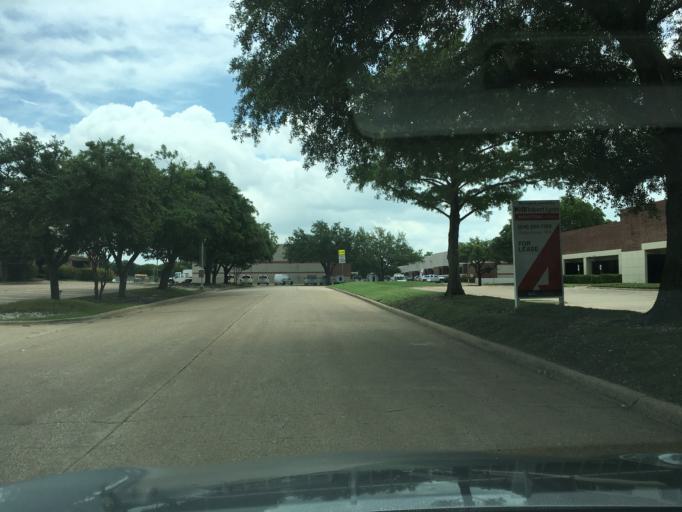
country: US
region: Texas
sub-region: Dallas County
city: Richardson
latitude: 32.9121
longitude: -96.7035
